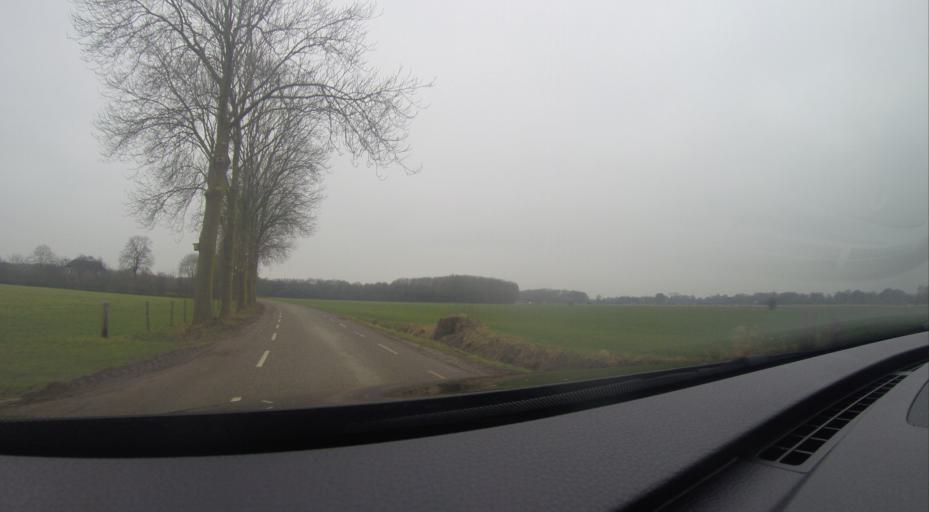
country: NL
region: Gelderland
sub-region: Gemeente Zutphen
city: Zutphen
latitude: 52.1205
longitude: 6.1740
